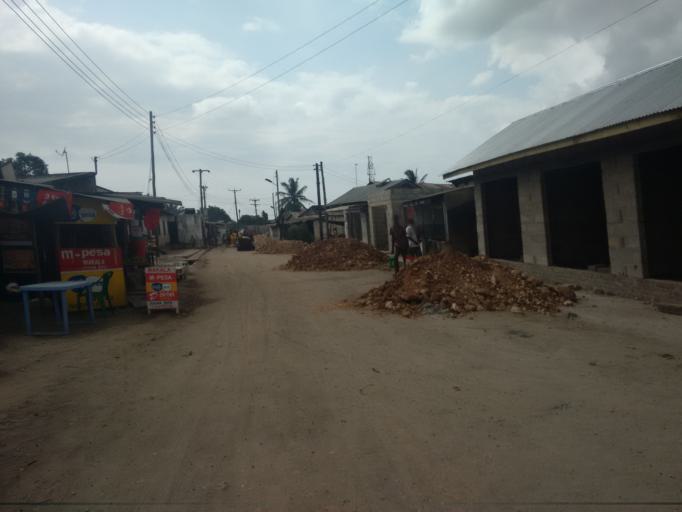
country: TZ
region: Dar es Salaam
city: Dar es Salaam
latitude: -6.8595
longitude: 39.2487
